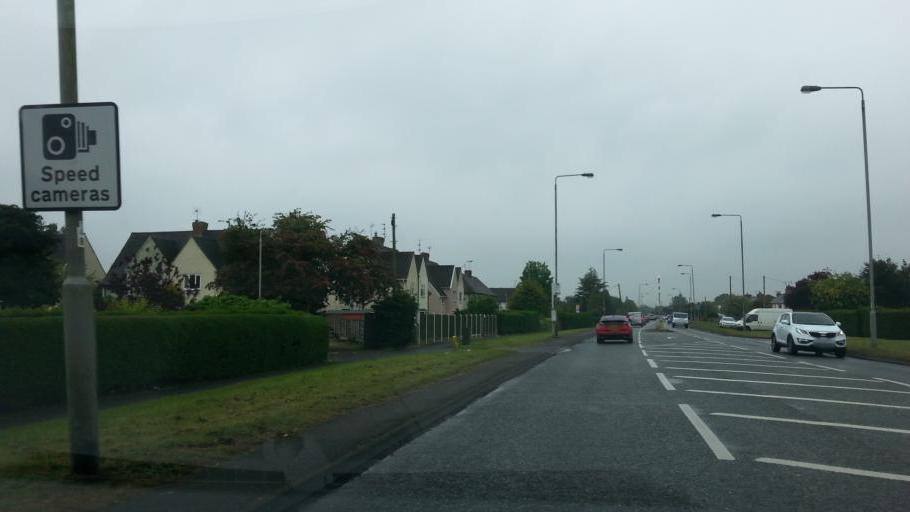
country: GB
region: England
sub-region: Nottinghamshire
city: Newark on Trent
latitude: 53.0898
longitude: -0.7920
